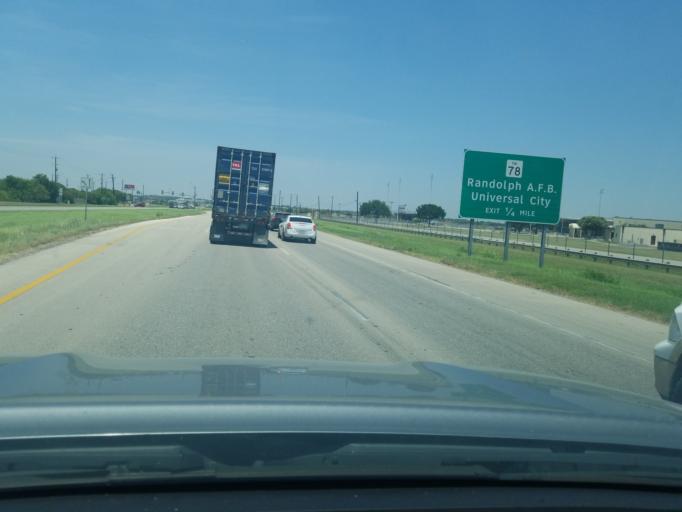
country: US
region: Texas
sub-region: Bexar County
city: Converse
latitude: 29.5264
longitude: -98.2962
